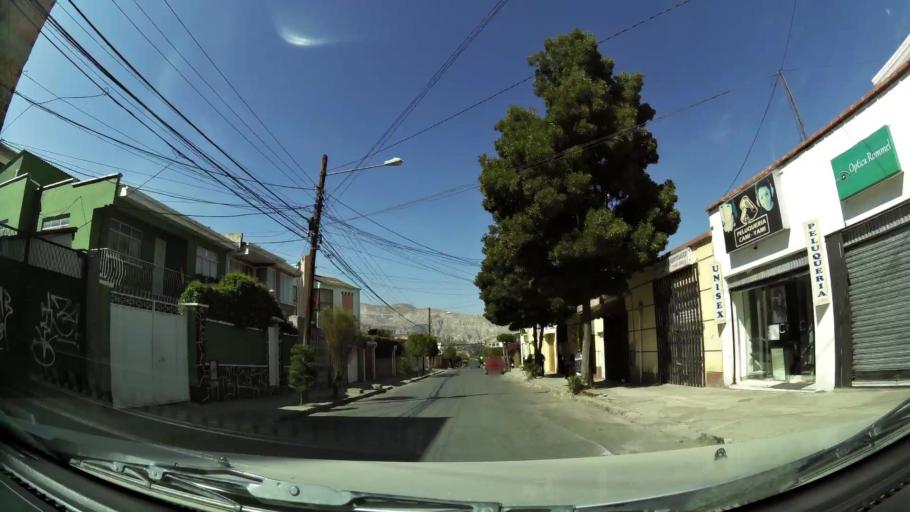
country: BO
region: La Paz
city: La Paz
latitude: -16.5237
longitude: -68.0865
